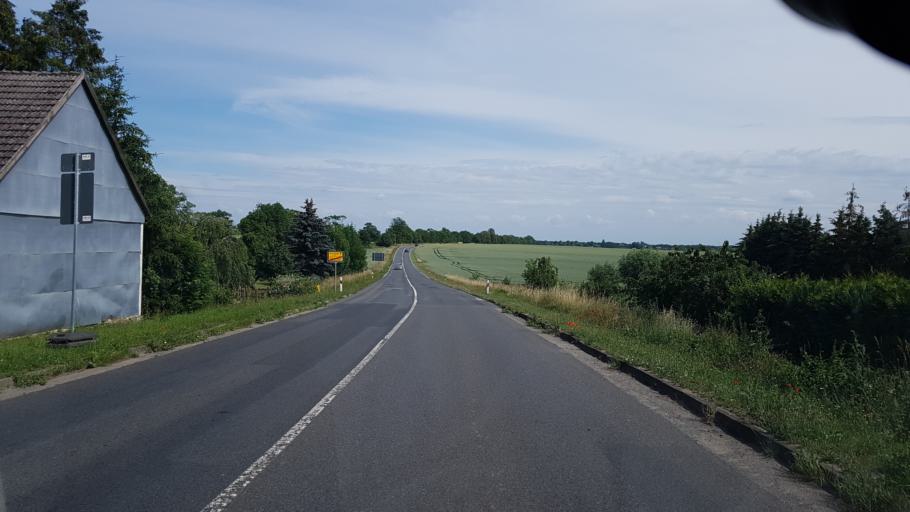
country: DE
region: Brandenburg
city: Prenzlau
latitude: 53.3222
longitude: 13.7875
